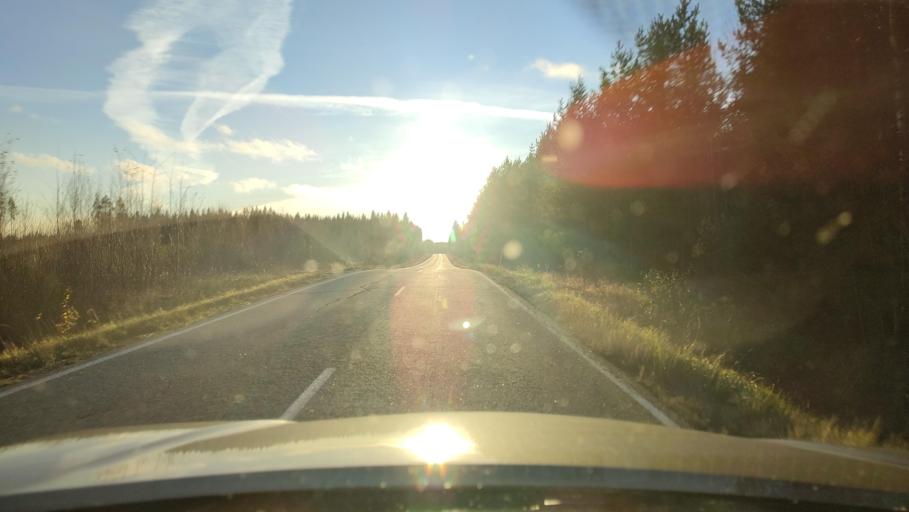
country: FI
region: Ostrobothnia
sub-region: Vaasa
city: Malax
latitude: 62.6944
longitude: 21.5647
